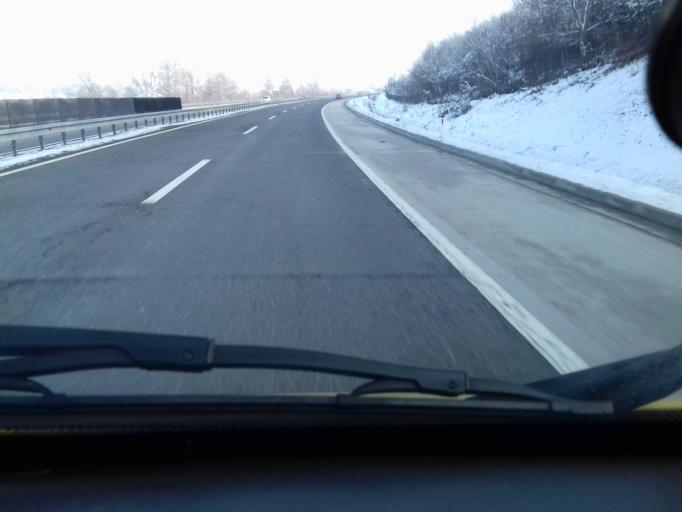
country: BA
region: Federation of Bosnia and Herzegovina
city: Visoko
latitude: 43.9929
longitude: 18.2143
